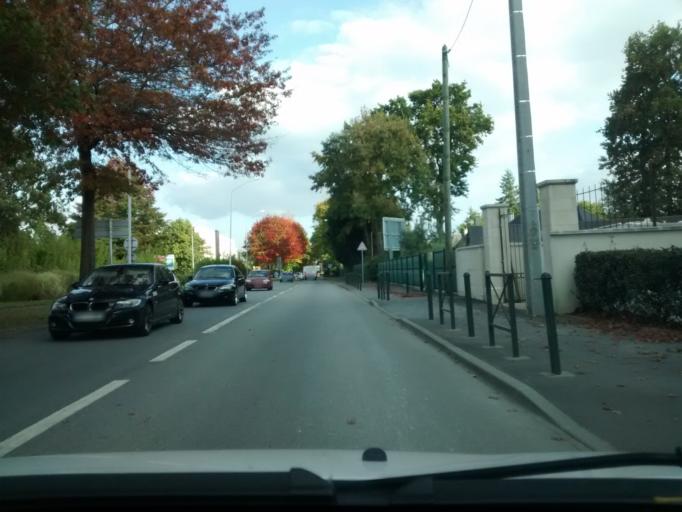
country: FR
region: Pays de la Loire
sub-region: Departement de la Loire-Atlantique
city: Orvault
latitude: 47.2606
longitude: -1.5865
